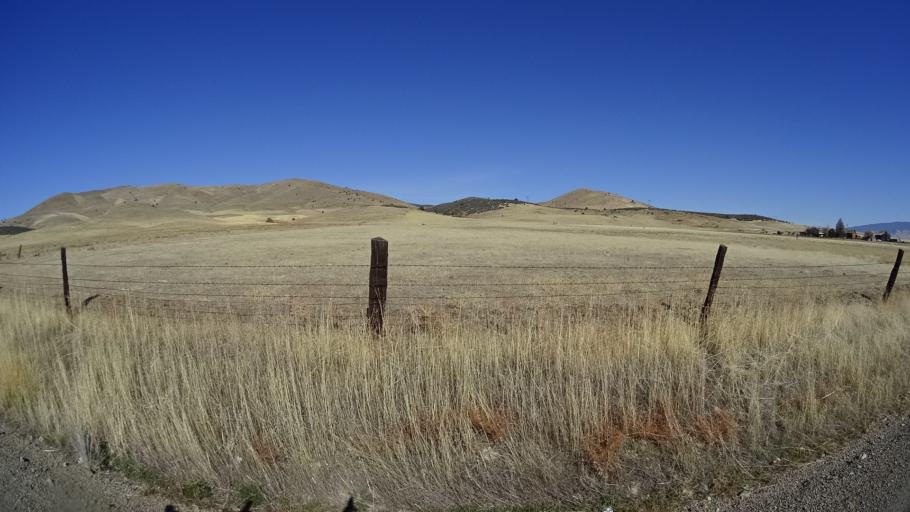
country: US
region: California
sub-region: Siskiyou County
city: Montague
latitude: 41.7713
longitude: -122.5337
